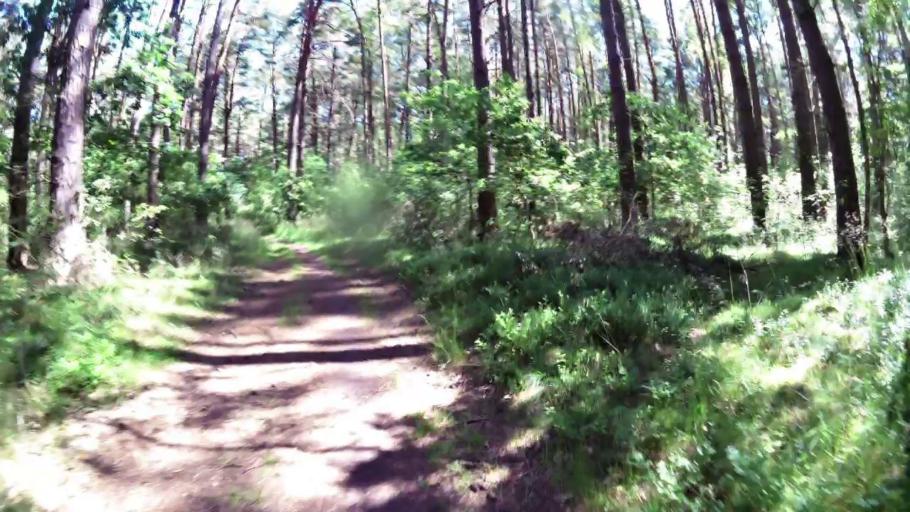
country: PL
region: West Pomeranian Voivodeship
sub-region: Powiat kamienski
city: Dziwnow
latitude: 54.0412
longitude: 14.8454
